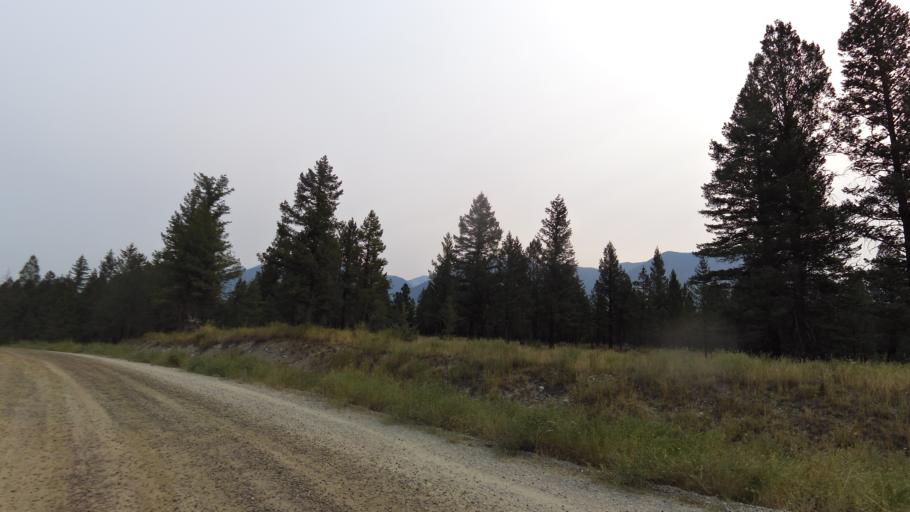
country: CA
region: British Columbia
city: Invermere
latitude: 50.5300
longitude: -116.0213
